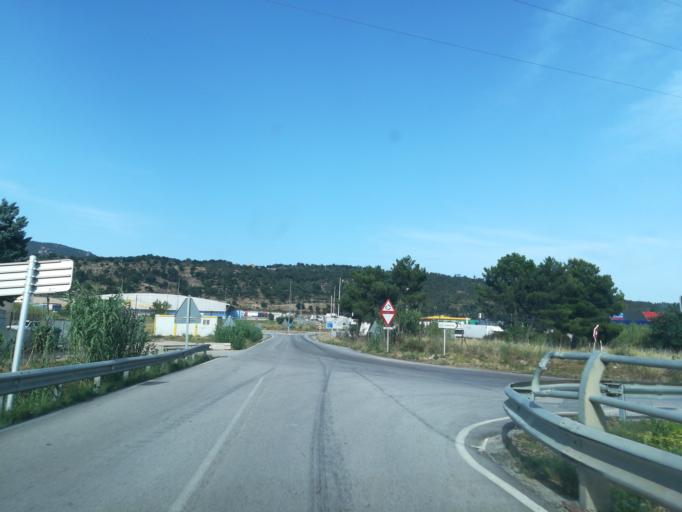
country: ES
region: Catalonia
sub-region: Provincia de Girona
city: la Jonquera
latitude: 42.4039
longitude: 2.8765
